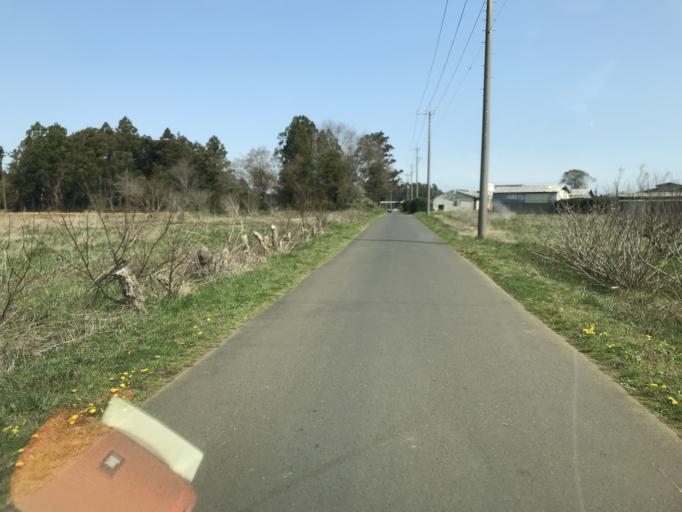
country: JP
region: Chiba
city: Sawara
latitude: 35.8391
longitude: 140.5239
